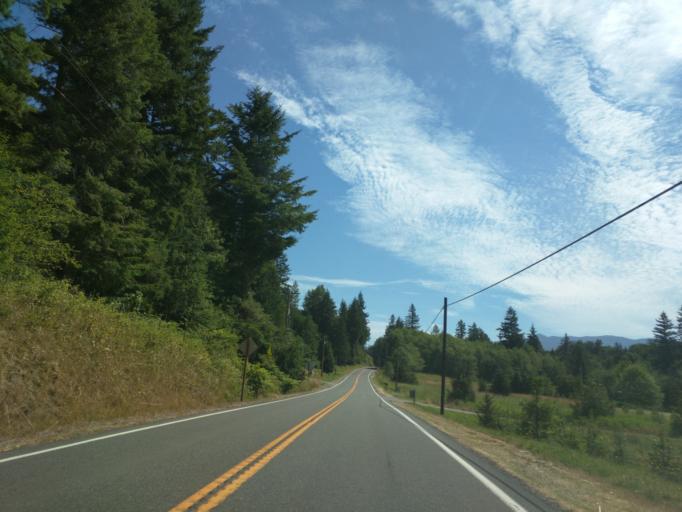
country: US
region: Washington
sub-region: Whatcom County
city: Sumas
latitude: 48.9655
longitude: -122.2205
